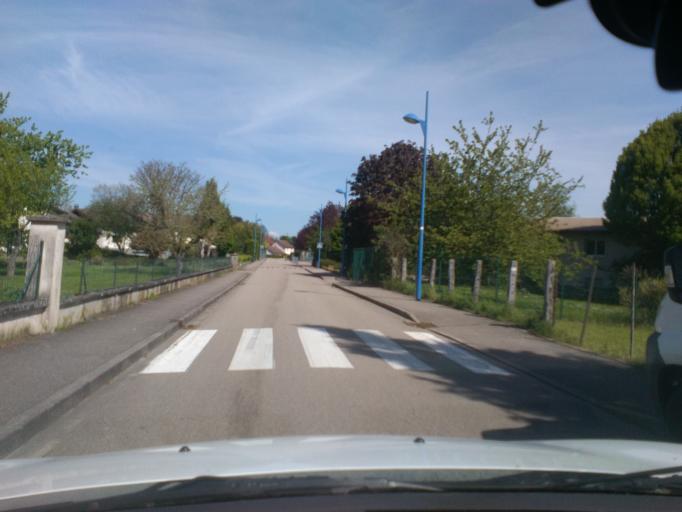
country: FR
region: Lorraine
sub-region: Departement des Vosges
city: Mirecourt
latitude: 48.2942
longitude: 6.1379
